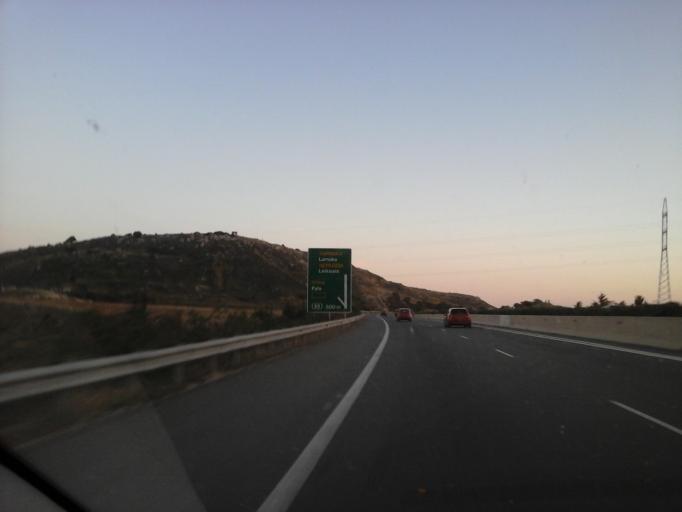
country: CY
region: Larnaka
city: Pyla
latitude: 35.0009
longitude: 33.7009
